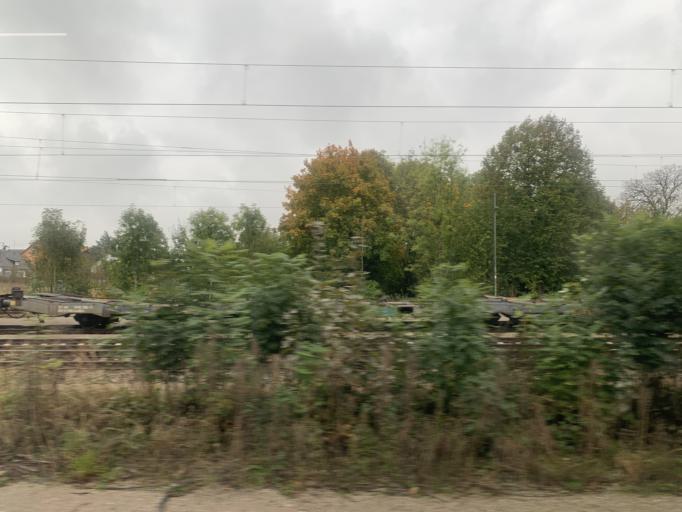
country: DE
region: Bavaria
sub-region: Upper Bavaria
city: Oberschleissheim
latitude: 48.2157
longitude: 11.5414
